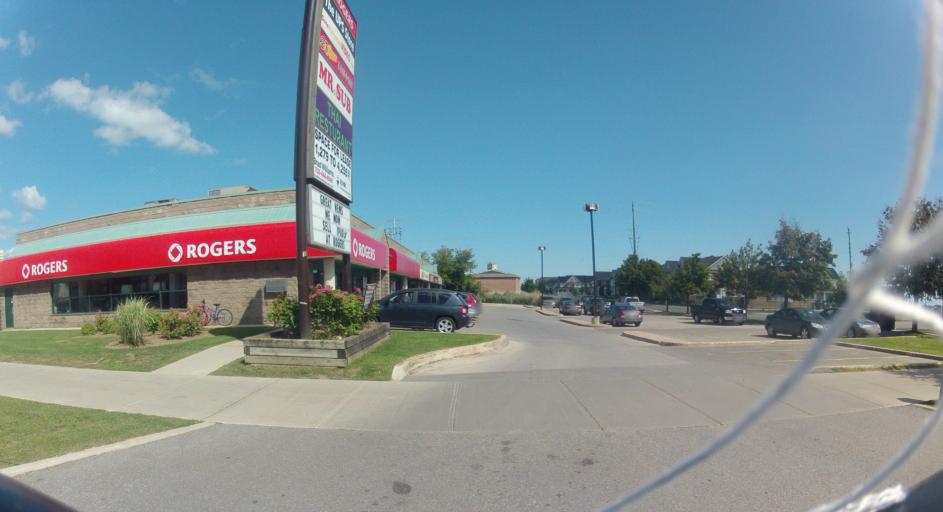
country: CA
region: Ontario
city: Collingwood
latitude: 44.5025
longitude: -80.2211
